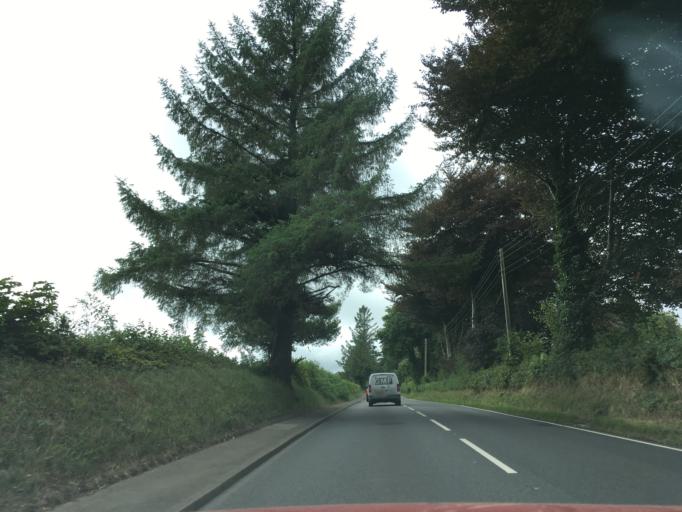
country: GB
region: Wales
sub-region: Carmarthenshire
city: Llanddarog
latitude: 51.8740
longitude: -4.1761
